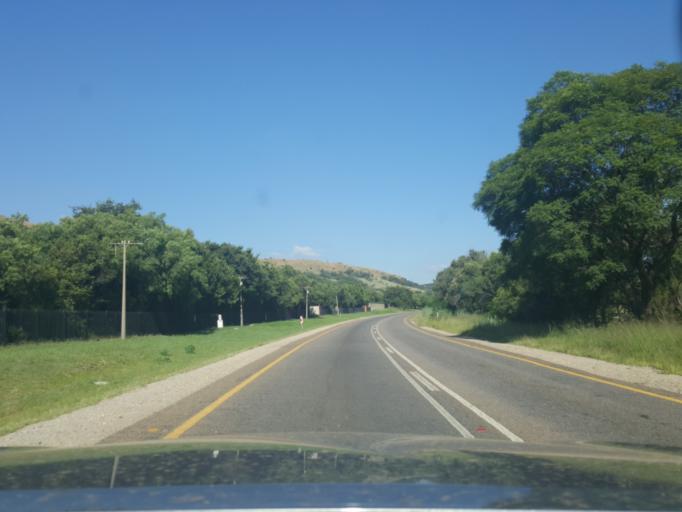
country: ZA
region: Gauteng
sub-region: City of Tshwane Metropolitan Municipality
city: Cullinan
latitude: -25.7749
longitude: 28.4634
